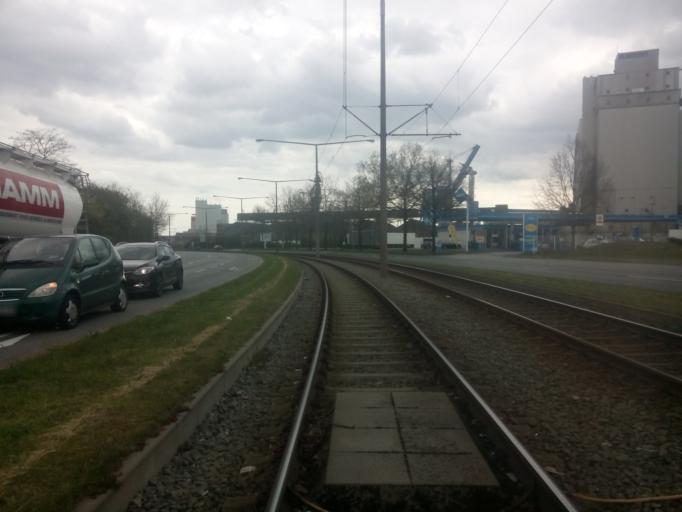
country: DE
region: Bremen
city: Bremen
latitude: 53.1119
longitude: 8.7529
